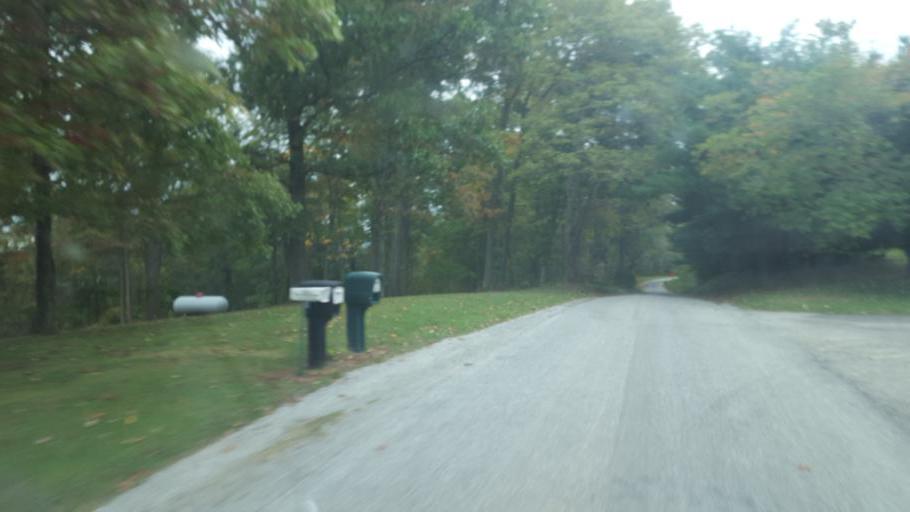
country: US
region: Ohio
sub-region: Harrison County
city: Cadiz
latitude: 40.3731
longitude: -81.0472
